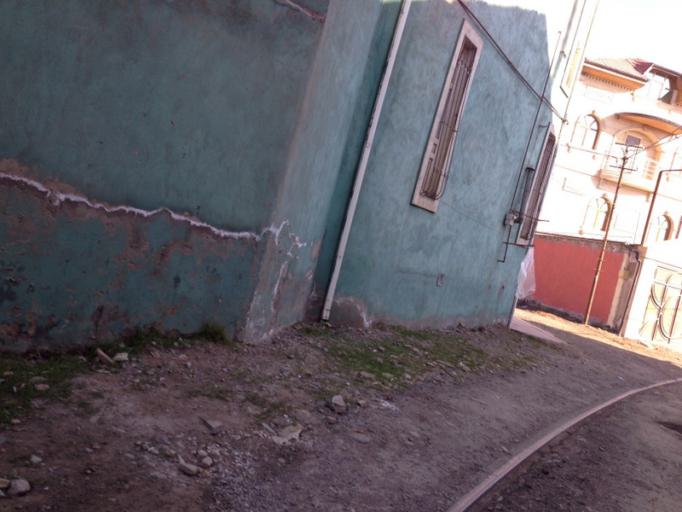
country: AZ
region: Baki
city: Baku
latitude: 40.4205
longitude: 49.8663
